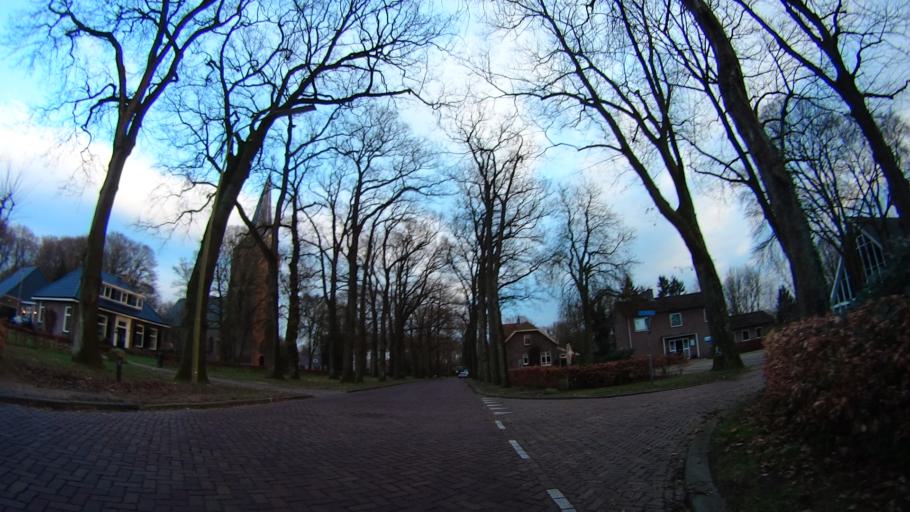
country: NL
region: Drenthe
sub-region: Gemeente Coevorden
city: Sleen
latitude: 52.7764
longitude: 6.8013
